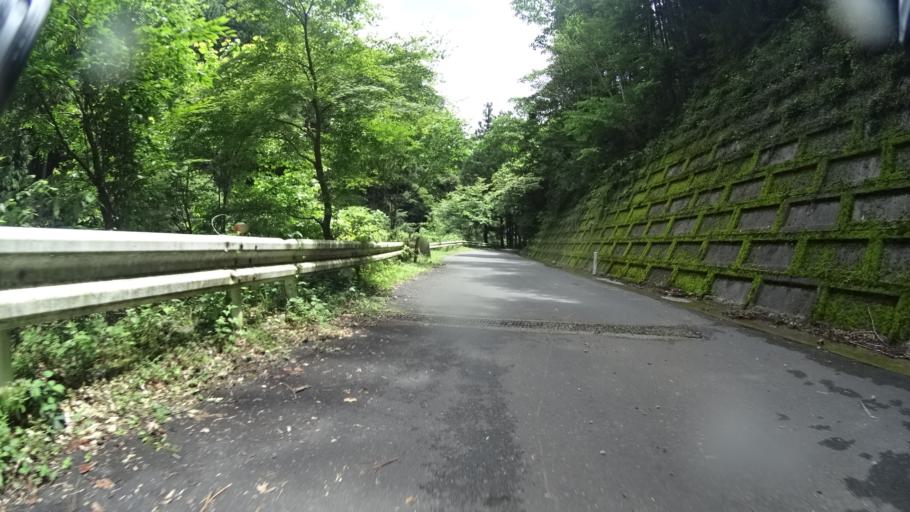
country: JP
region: Saitama
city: Chichibu
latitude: 35.8776
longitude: 139.1468
